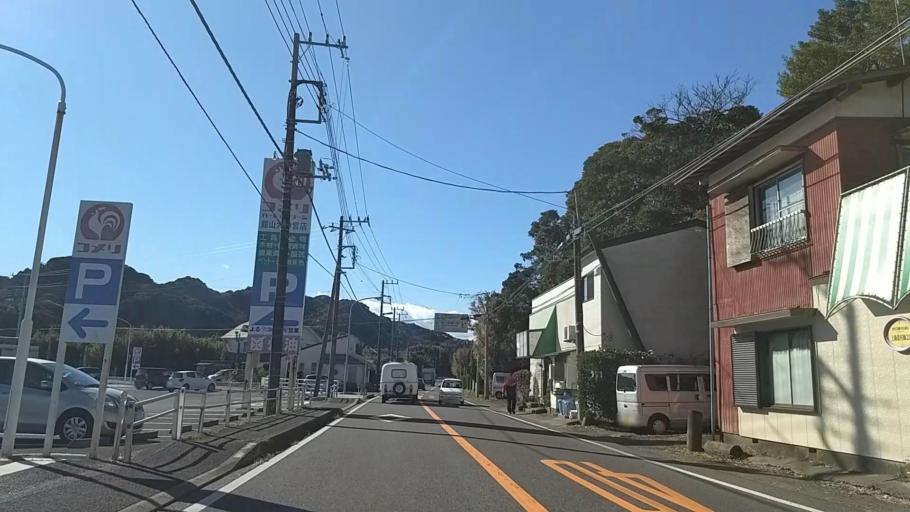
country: JP
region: Chiba
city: Tateyama
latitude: 34.9288
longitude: 139.8365
